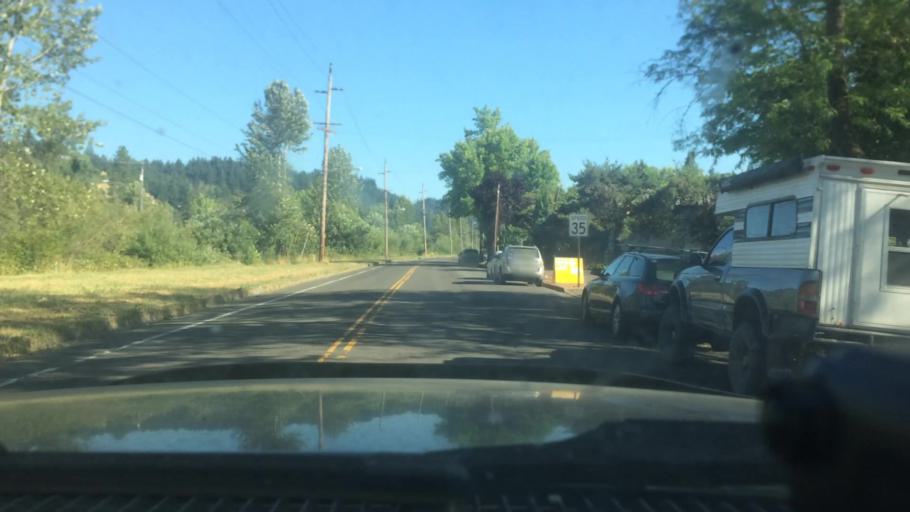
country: US
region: Oregon
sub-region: Lane County
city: Eugene
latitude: 44.0193
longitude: -123.0807
